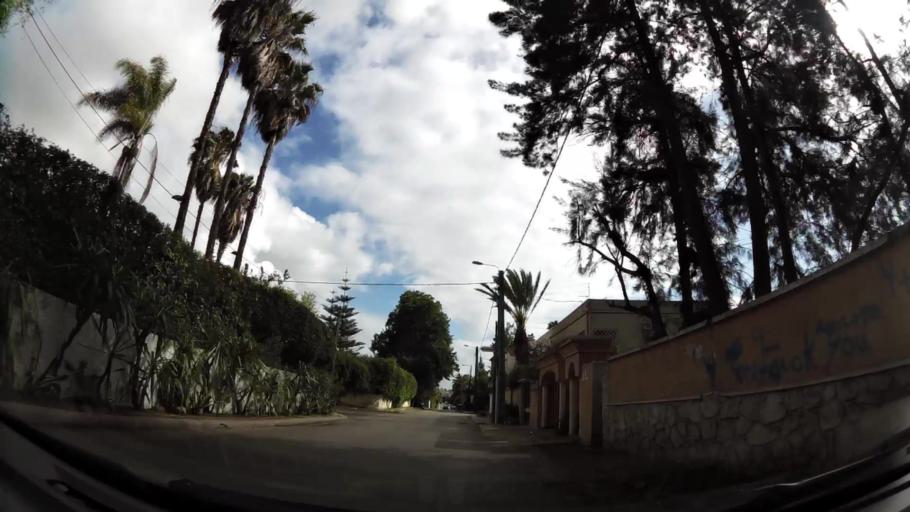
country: MA
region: Grand Casablanca
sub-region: Casablanca
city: Casablanca
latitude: 33.5458
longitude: -7.6252
